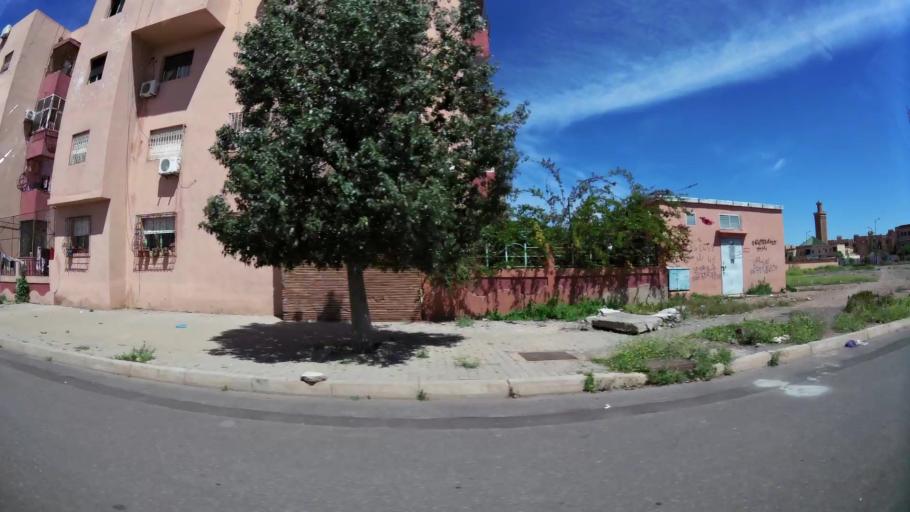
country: MA
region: Marrakech-Tensift-Al Haouz
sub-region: Marrakech
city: Marrakesh
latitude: 31.6401
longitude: -8.0810
